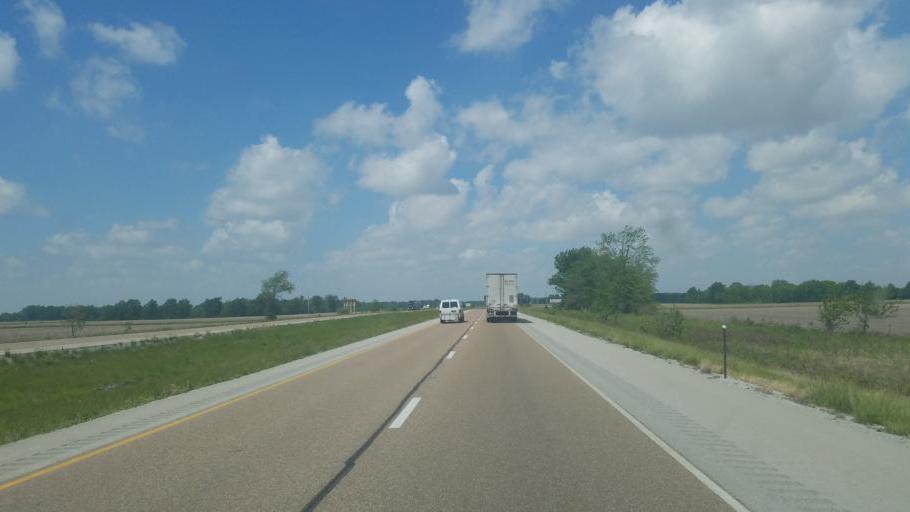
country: US
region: Illinois
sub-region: Cumberland County
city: Greenup
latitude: 39.2748
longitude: -88.0972
